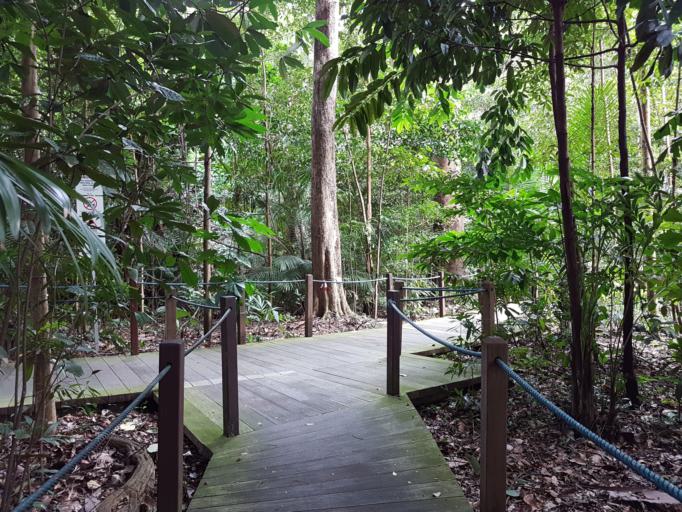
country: SG
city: Singapore
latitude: 1.3141
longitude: 103.8163
